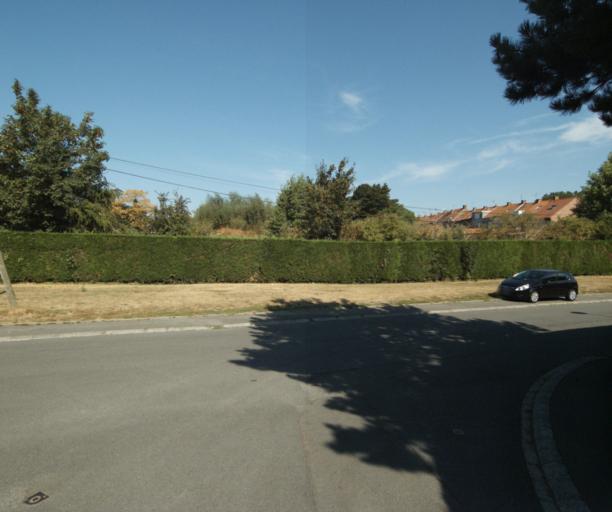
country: FR
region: Nord-Pas-de-Calais
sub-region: Departement du Nord
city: Halluin
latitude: 50.7793
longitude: 3.1342
